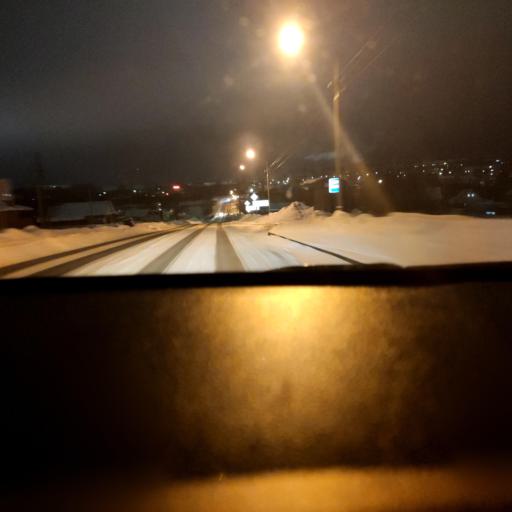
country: RU
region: Tatarstan
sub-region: Chistopol'skiy Rayon
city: Chistopol'
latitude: 55.3580
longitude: 50.6175
